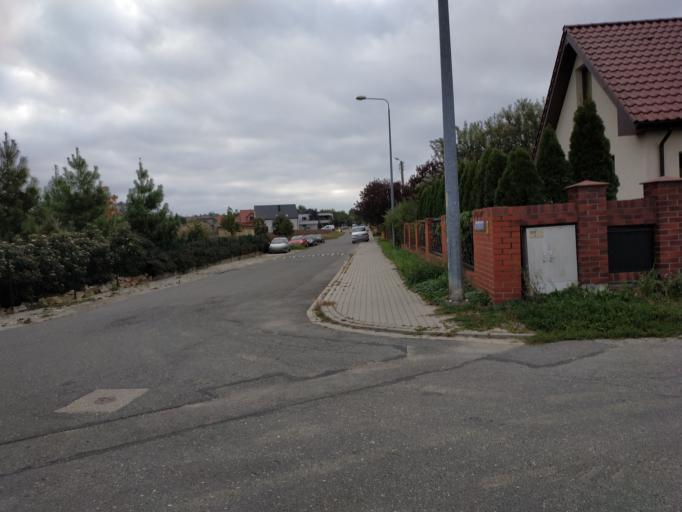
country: PL
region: Lower Silesian Voivodeship
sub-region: Powiat wroclawski
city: Tyniec Maly
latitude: 51.0214
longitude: 16.9117
